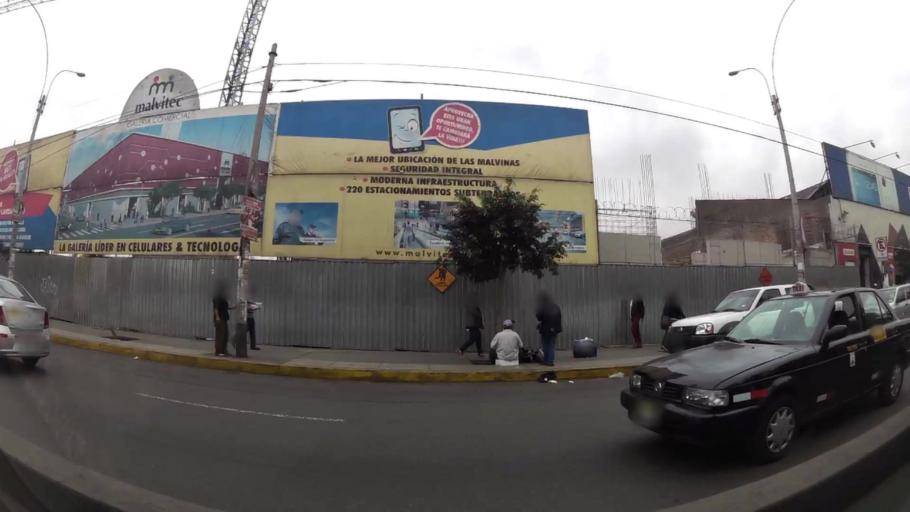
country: PE
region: Lima
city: Lima
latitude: -12.0429
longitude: -77.0480
